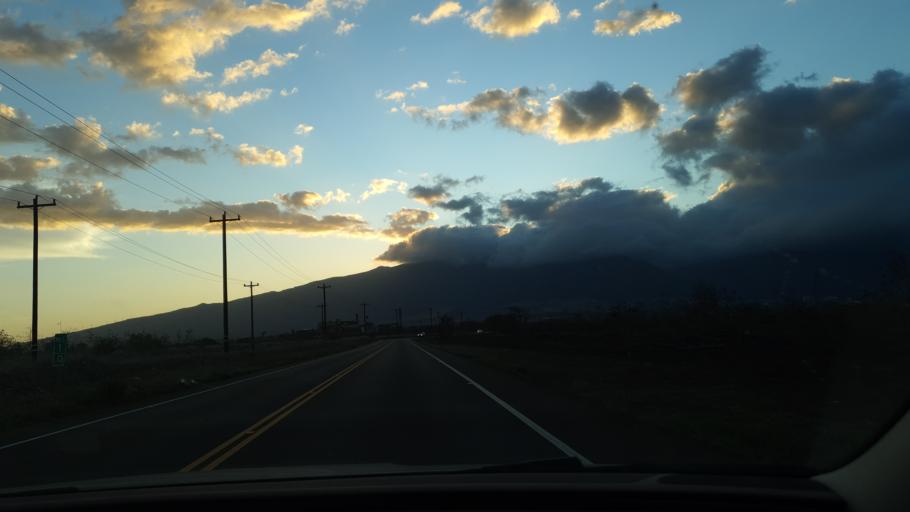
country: US
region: Hawaii
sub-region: Maui County
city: Kahului
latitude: 20.8716
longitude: -156.4423
